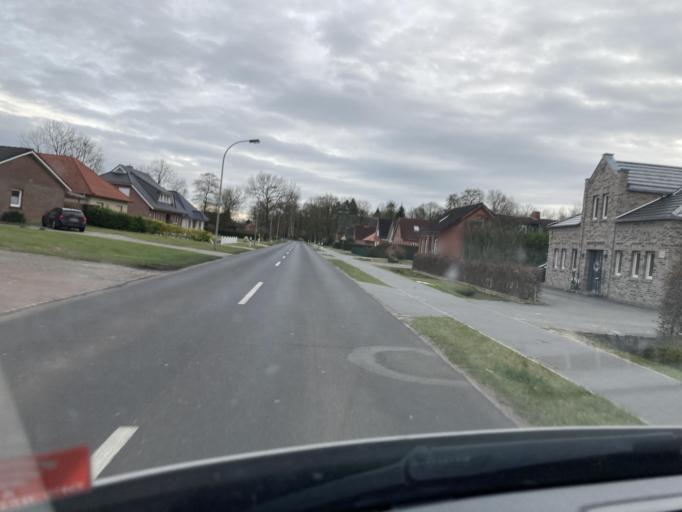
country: DE
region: Lower Saxony
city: Leer
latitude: 53.1461
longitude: 7.4730
